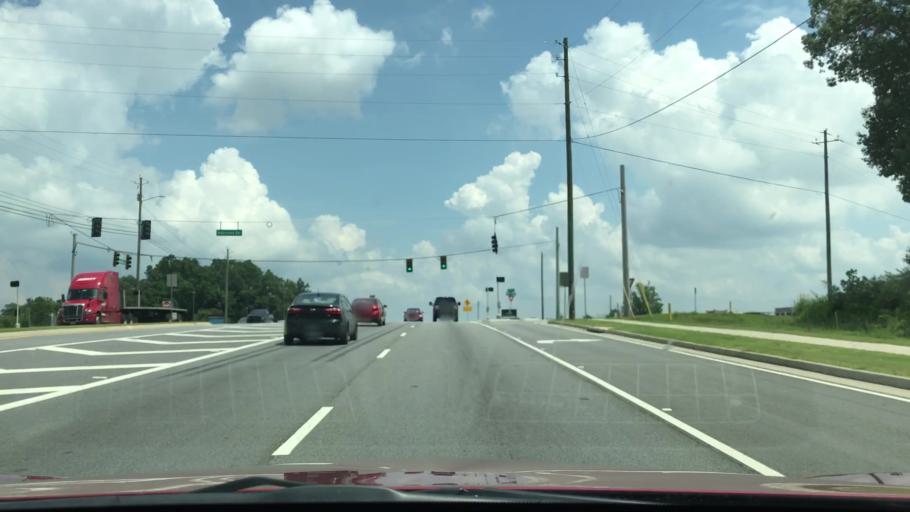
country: US
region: Georgia
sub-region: Gwinnett County
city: Sugar Hill
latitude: 34.1100
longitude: -84.0368
